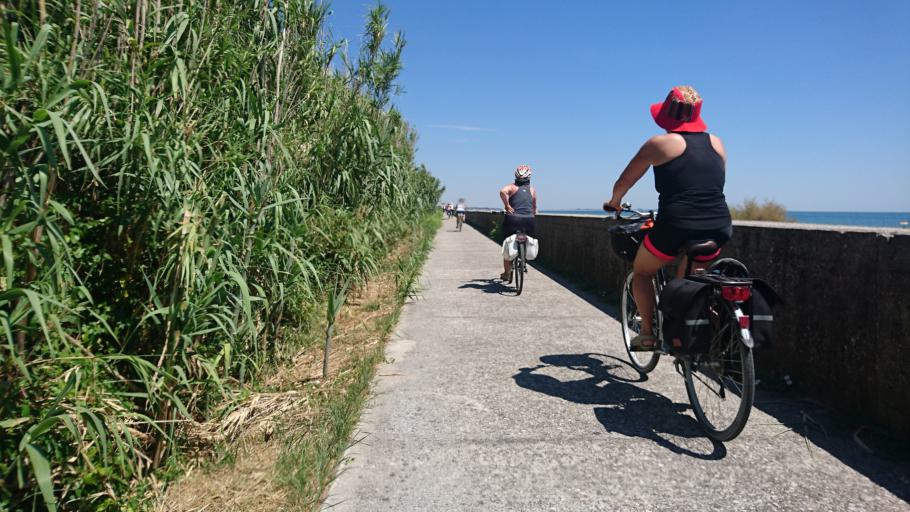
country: IT
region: Veneto
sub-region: Provincia di Venezia
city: Lido
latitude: 45.3809
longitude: 12.3490
